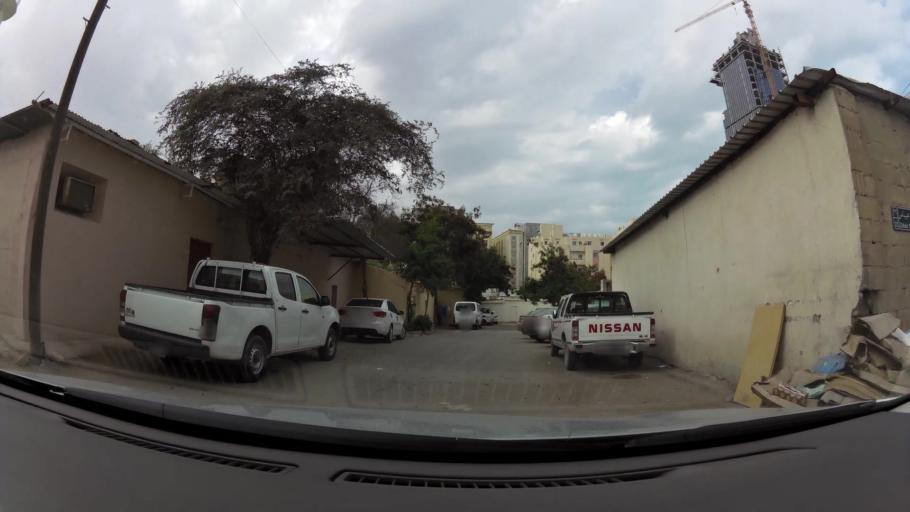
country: QA
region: Baladiyat ad Dawhah
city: Doha
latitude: 25.2840
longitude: 51.5158
